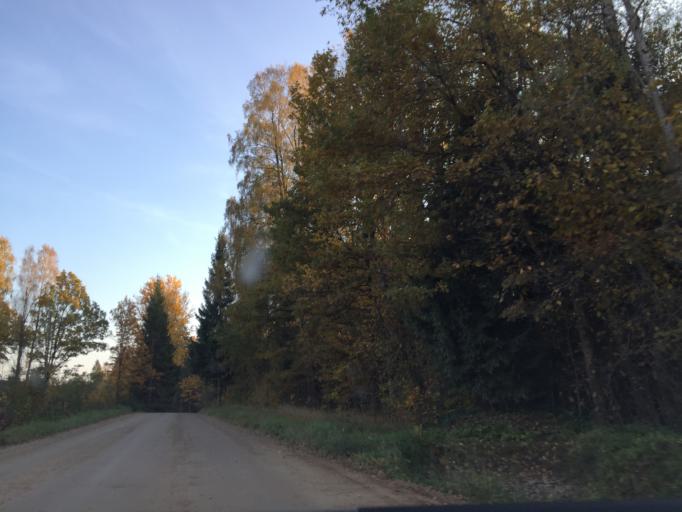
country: LV
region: Vainode
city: Vainode
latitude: 56.6022
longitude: 21.8245
